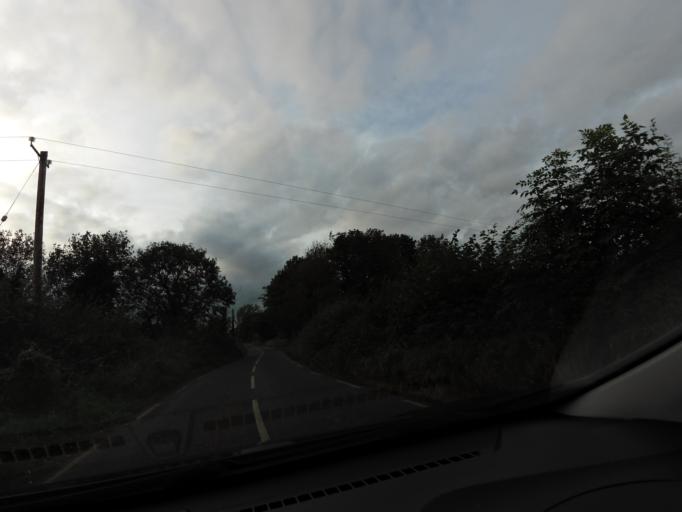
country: IE
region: Leinster
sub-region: Uibh Fhaili
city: Ferbane
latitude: 53.1874
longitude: -7.7511
